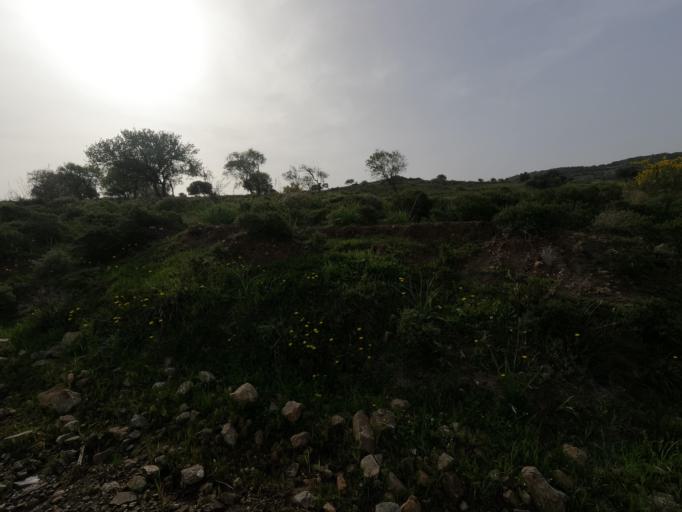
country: CY
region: Pafos
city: Pegeia
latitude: 34.9499
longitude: 32.3674
